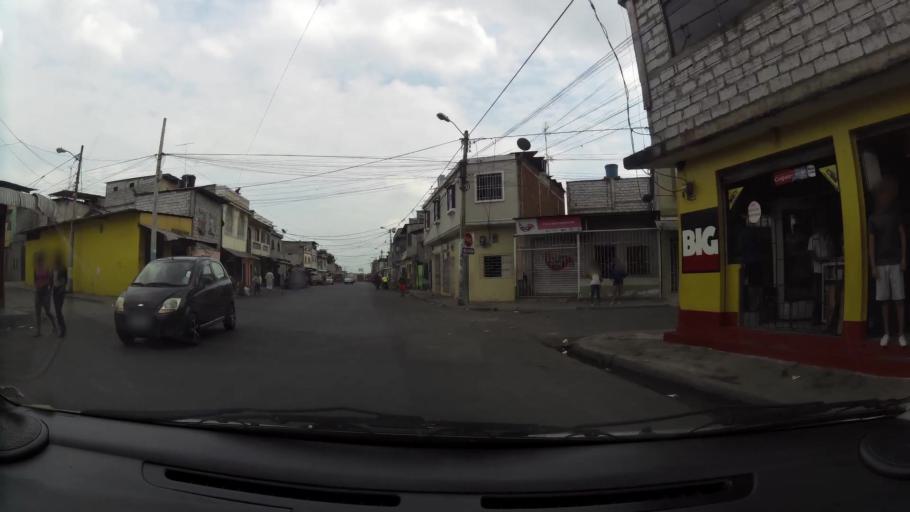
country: EC
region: Guayas
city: Guayaquil
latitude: -2.2302
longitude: -79.9118
